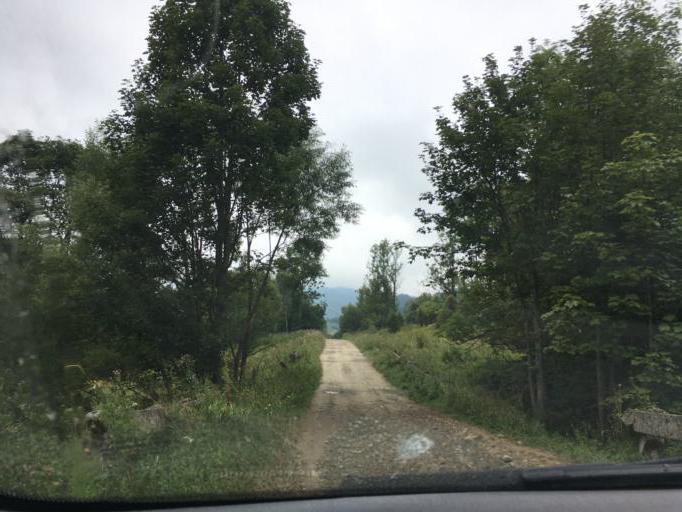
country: PL
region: Subcarpathian Voivodeship
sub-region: Powiat bieszczadzki
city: Lutowiska
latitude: 49.1613
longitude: 22.6266
